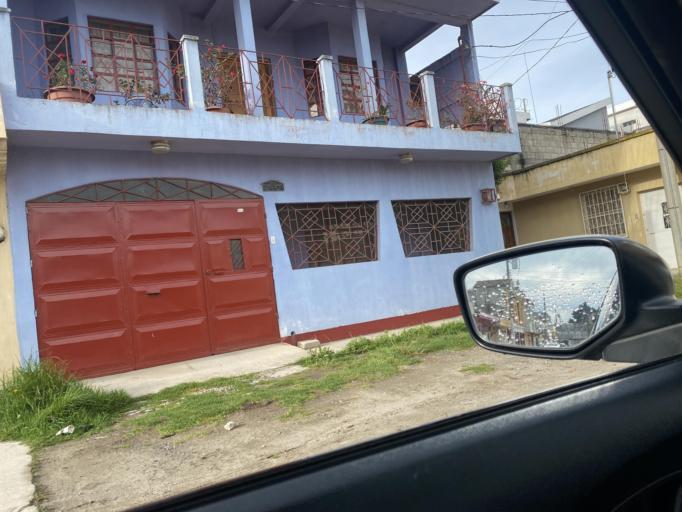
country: GT
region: Quetzaltenango
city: Olintepeque
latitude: 14.8647
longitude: -91.5230
